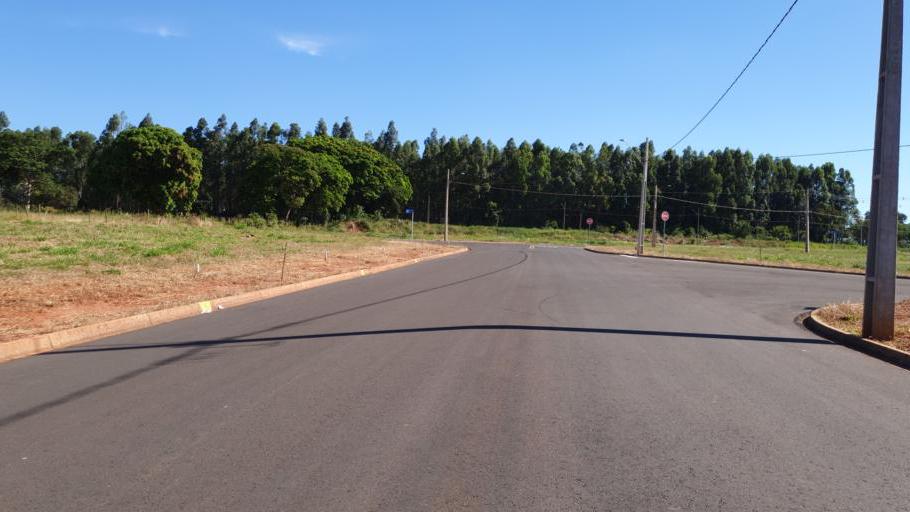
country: BR
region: Sao Paulo
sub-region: Paraguacu Paulista
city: Paraguacu Paulista
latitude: -22.4001
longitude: -50.5776
